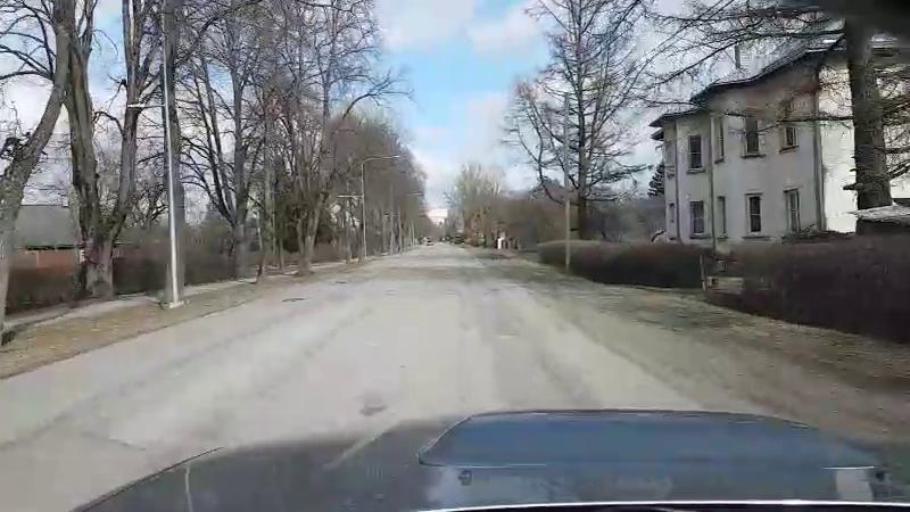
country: EE
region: Jaervamaa
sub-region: Paide linn
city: Paide
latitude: 58.8849
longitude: 25.5489
